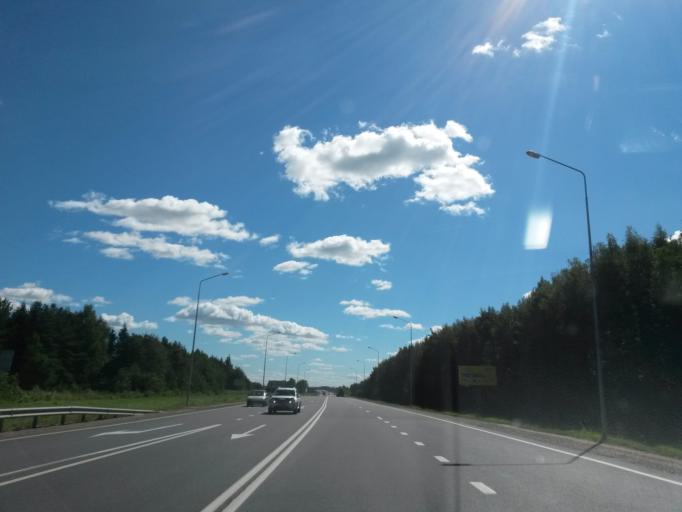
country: RU
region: Jaroslavl
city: Yaroslavl
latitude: 57.7347
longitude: 39.8965
